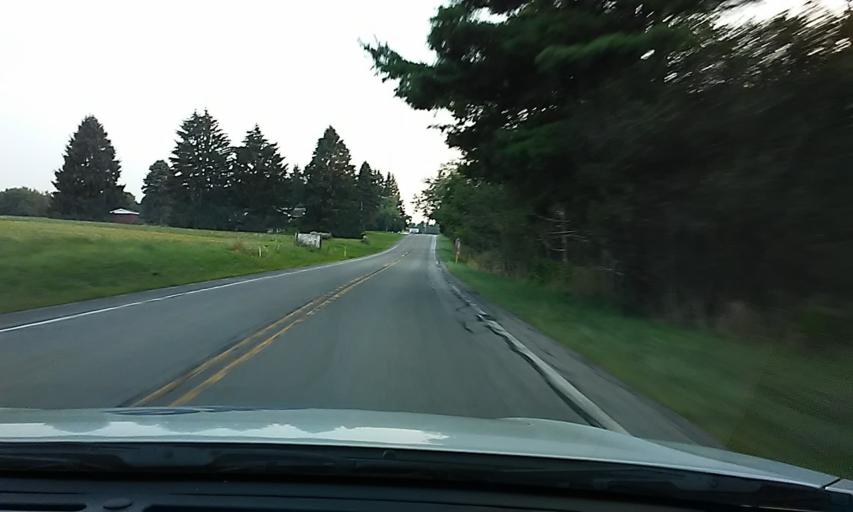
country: US
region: Pennsylvania
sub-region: Clarion County
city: Marianne
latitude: 41.2616
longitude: -79.3925
